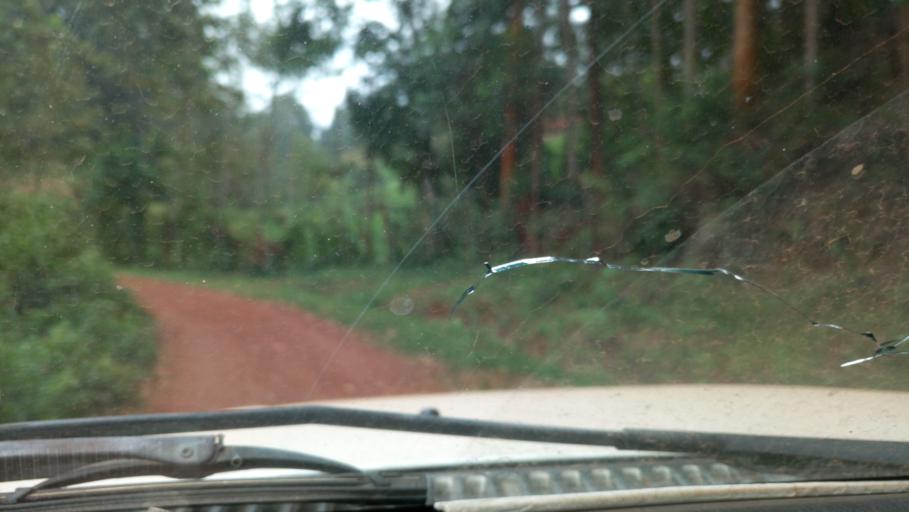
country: KE
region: Murang'a District
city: Kangema
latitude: -0.6750
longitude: 36.9614
